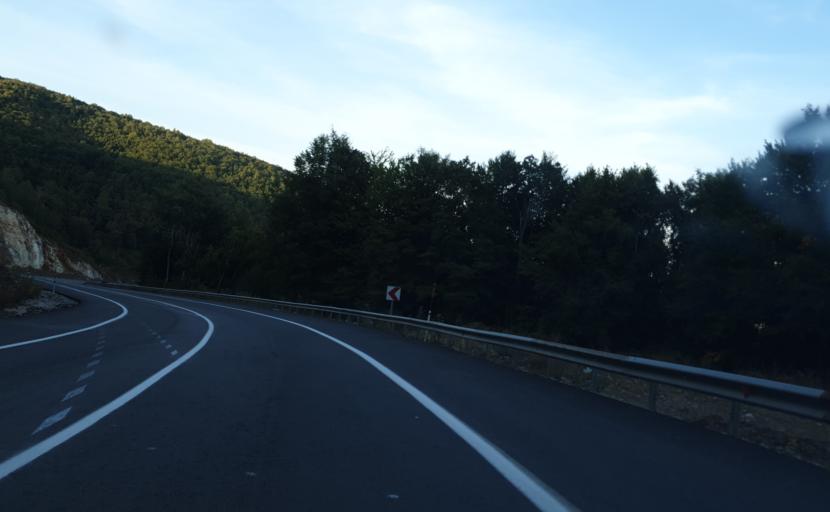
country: TR
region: Kirklareli
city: Sergen
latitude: 41.8080
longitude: 27.7388
